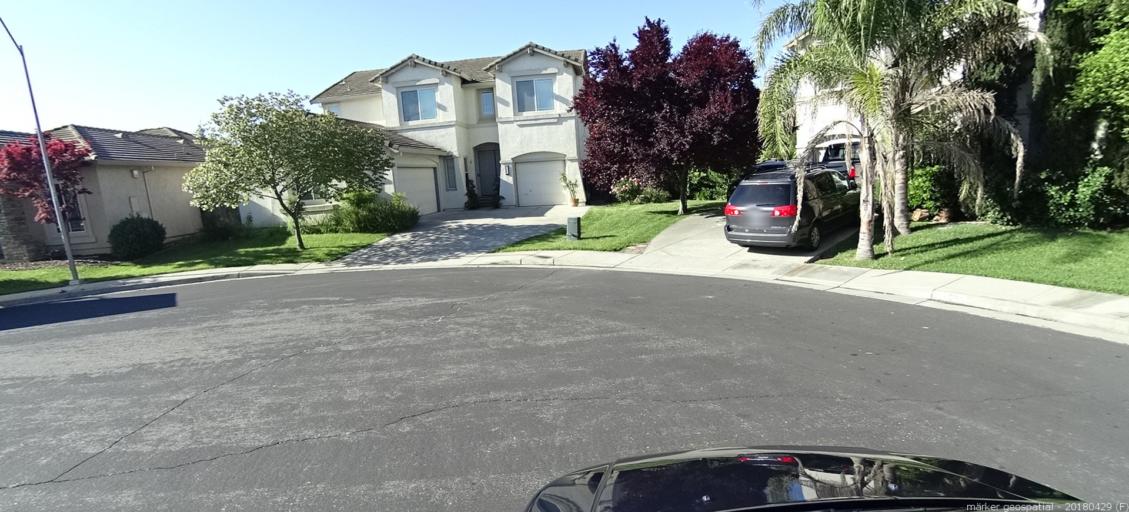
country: US
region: California
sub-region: Yolo County
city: West Sacramento
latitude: 38.5364
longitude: -121.5736
